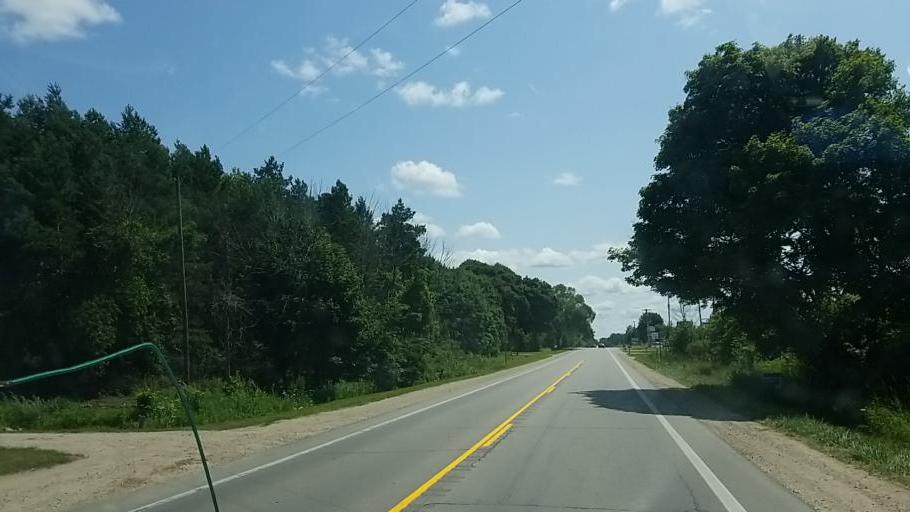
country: US
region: Michigan
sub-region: Newaygo County
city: Fremont
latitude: 43.4499
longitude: -85.9400
